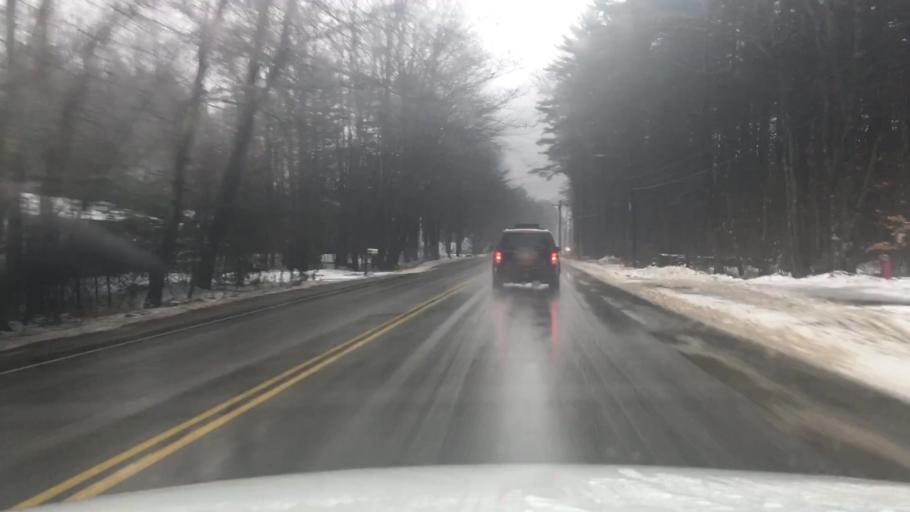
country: US
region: Maine
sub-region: Cumberland County
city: Westbrook
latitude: 43.6377
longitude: -70.3940
